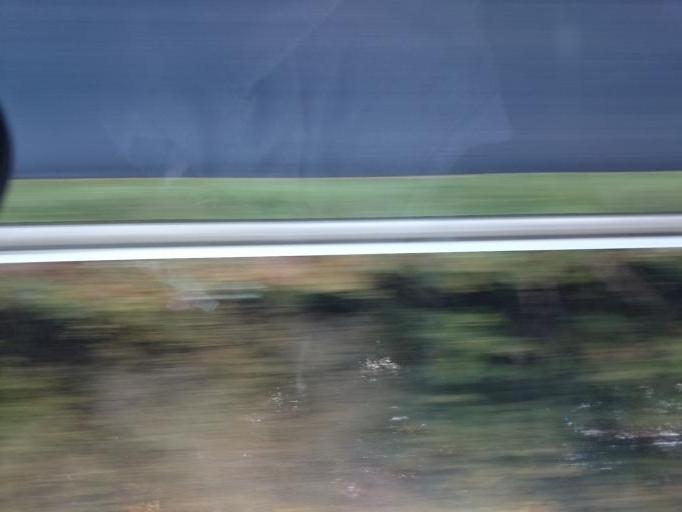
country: FR
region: Brittany
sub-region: Departement du Finistere
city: Plouigneau
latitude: 48.5771
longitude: -3.7305
